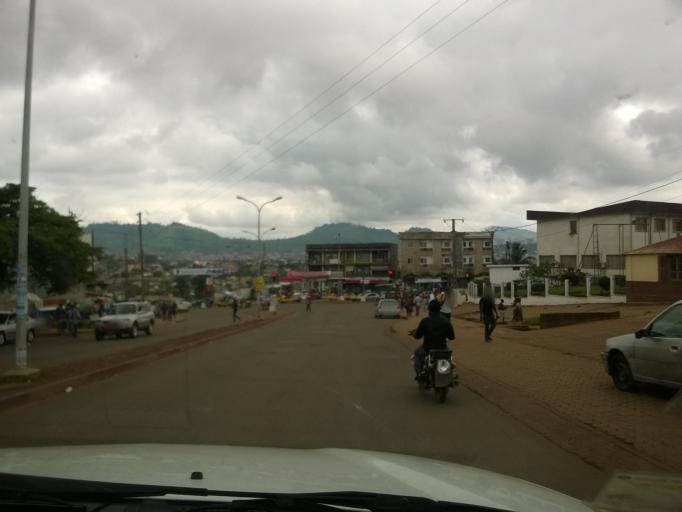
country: CM
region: Centre
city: Yaounde
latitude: 3.8617
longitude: 11.5045
